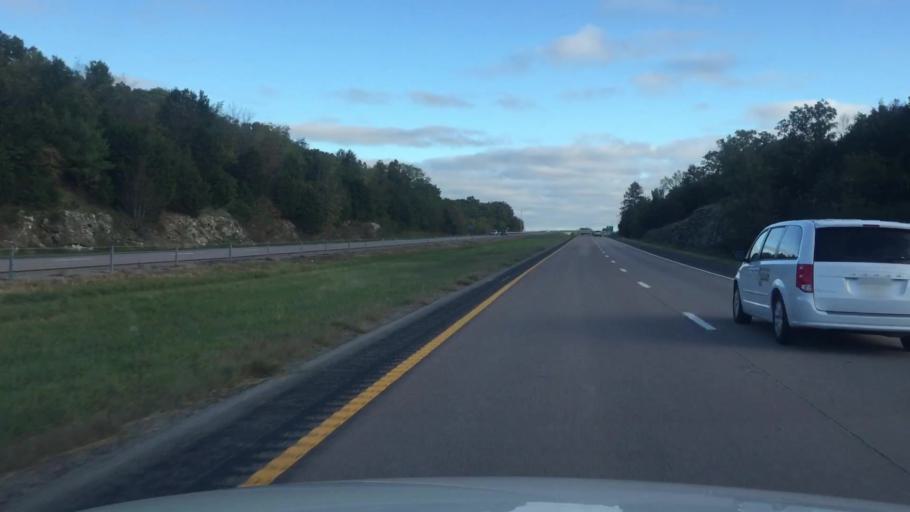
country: US
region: Missouri
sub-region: Boone County
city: Ashland
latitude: 38.8234
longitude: -92.2509
